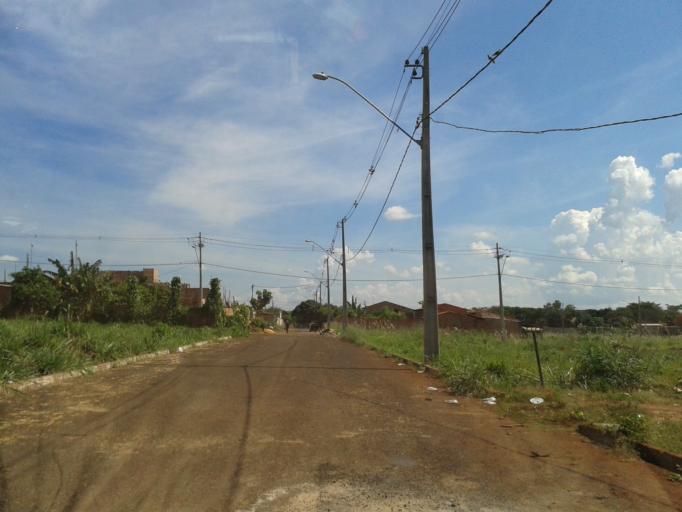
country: BR
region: Goias
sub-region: Itumbiara
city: Itumbiara
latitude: -18.4225
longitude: -49.1830
